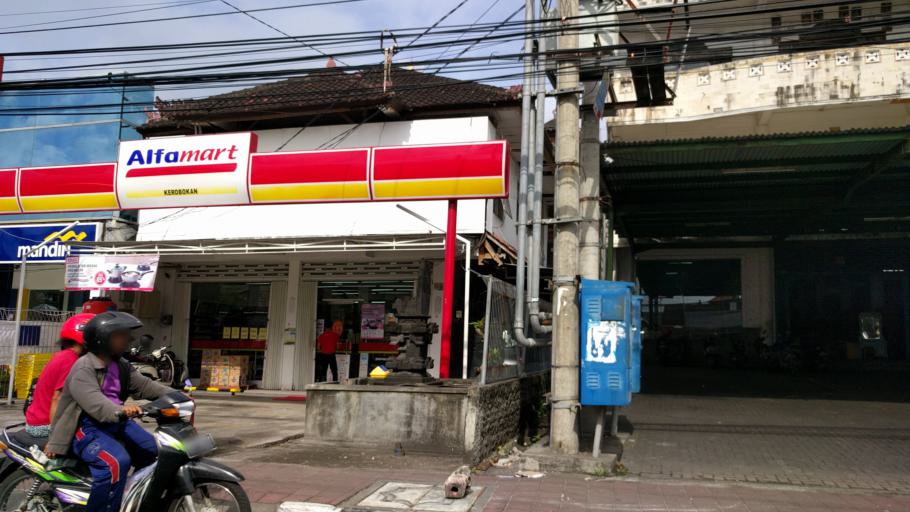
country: ID
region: Bali
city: Kuta
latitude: -8.6797
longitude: 115.1645
